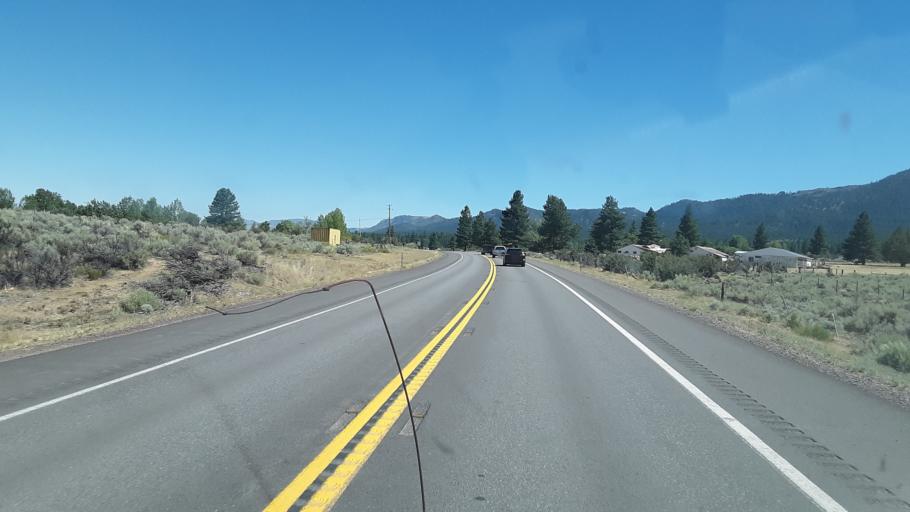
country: US
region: California
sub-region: Lassen County
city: Janesville
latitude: 40.3191
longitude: -120.5433
